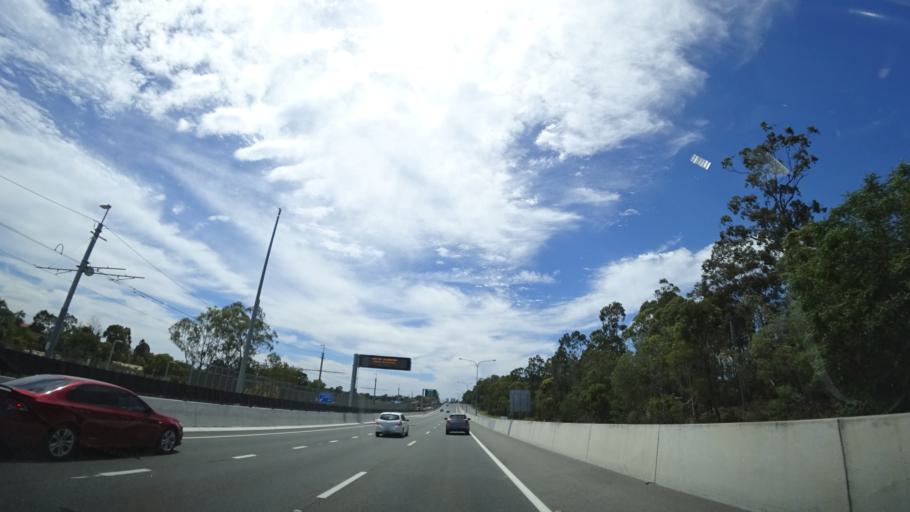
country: AU
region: Queensland
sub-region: Gold Coast
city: Nerang
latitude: -27.9626
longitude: 153.3609
